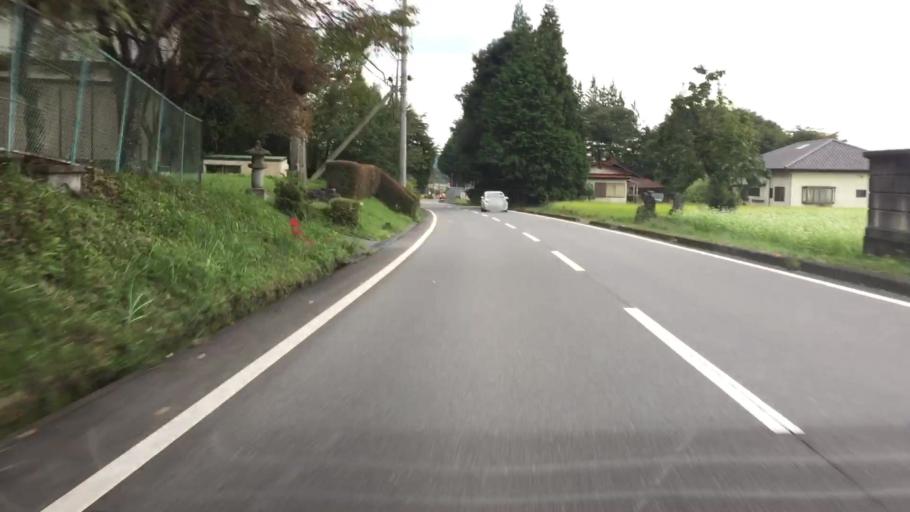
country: JP
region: Tochigi
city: Imaichi
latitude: 36.7669
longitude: 139.6906
